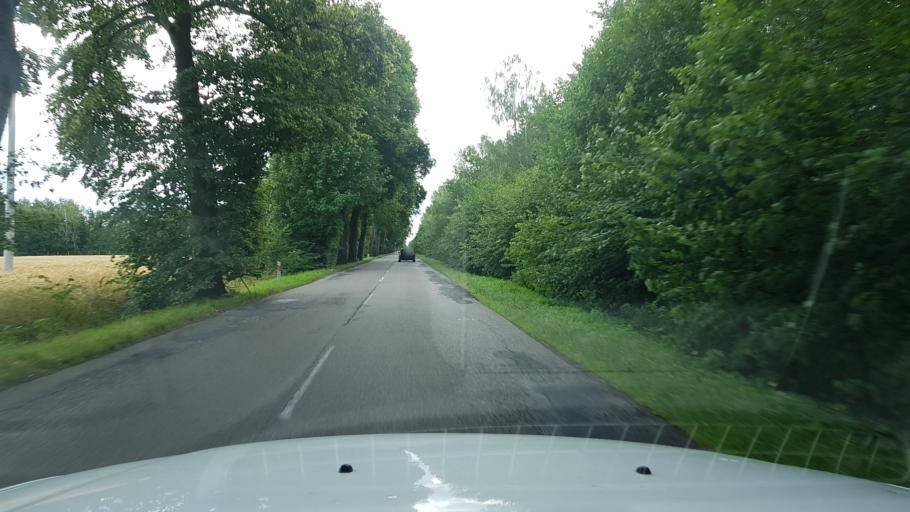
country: PL
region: West Pomeranian Voivodeship
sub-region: Powiat swidwinski
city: Rabino
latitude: 53.7760
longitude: 15.9473
